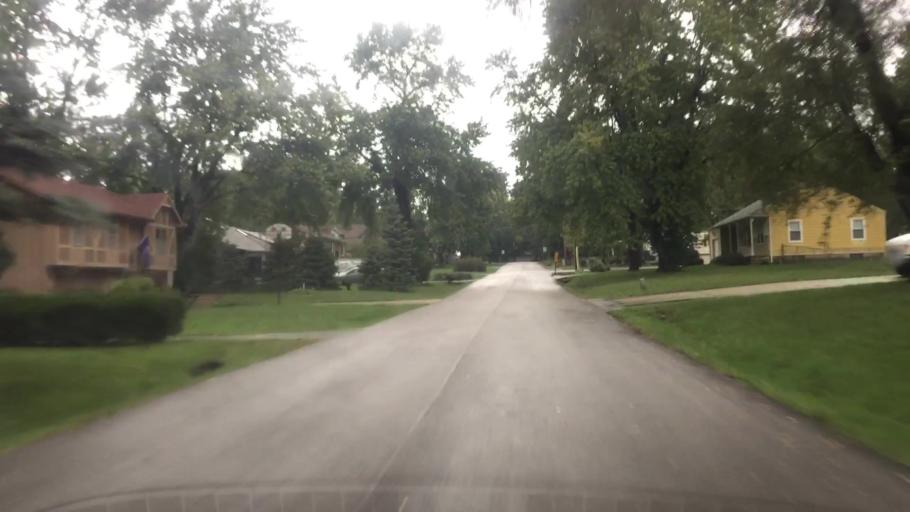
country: US
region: Kansas
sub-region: Johnson County
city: Shawnee
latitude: 39.0249
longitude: -94.7303
